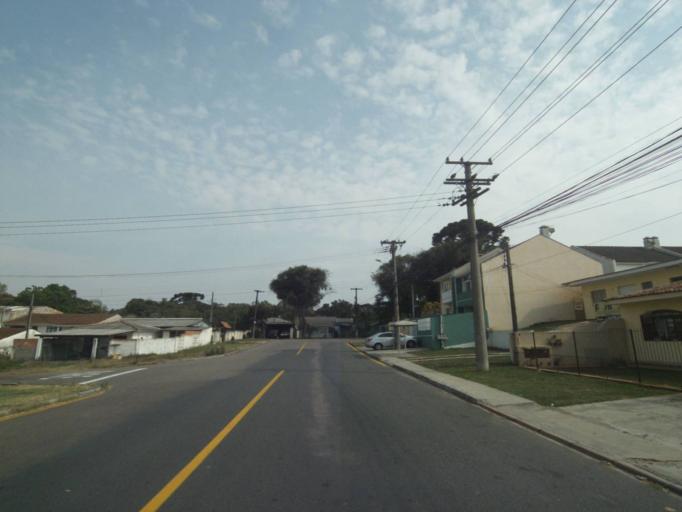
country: BR
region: Parana
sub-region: Pinhais
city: Pinhais
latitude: -25.4817
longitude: -49.2100
